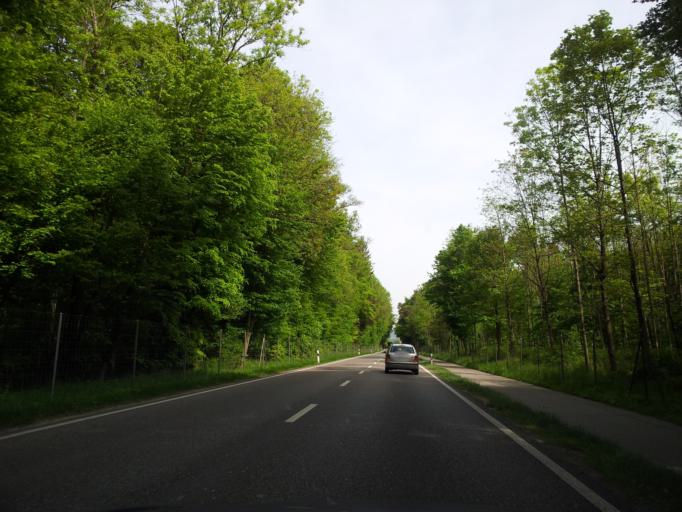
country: CH
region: Zurich
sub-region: Bezirk Buelach
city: Buelach / Soligaenter
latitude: 47.5447
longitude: 8.5309
